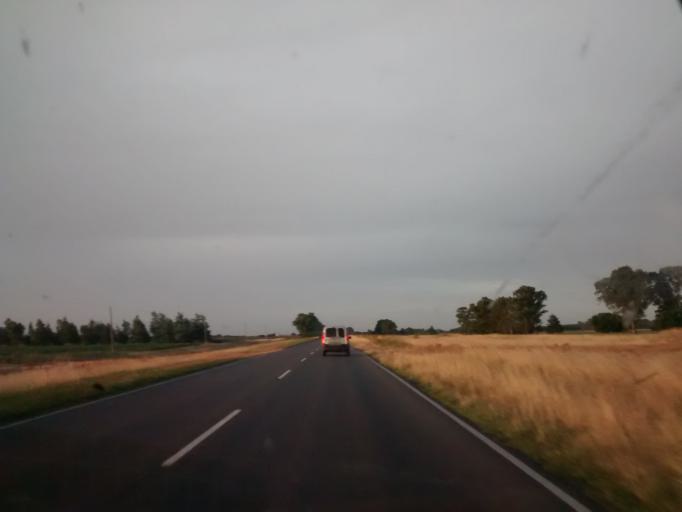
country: AR
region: Buenos Aires
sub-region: Partido de General Belgrano
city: General Belgrano
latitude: -35.8986
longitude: -58.6188
